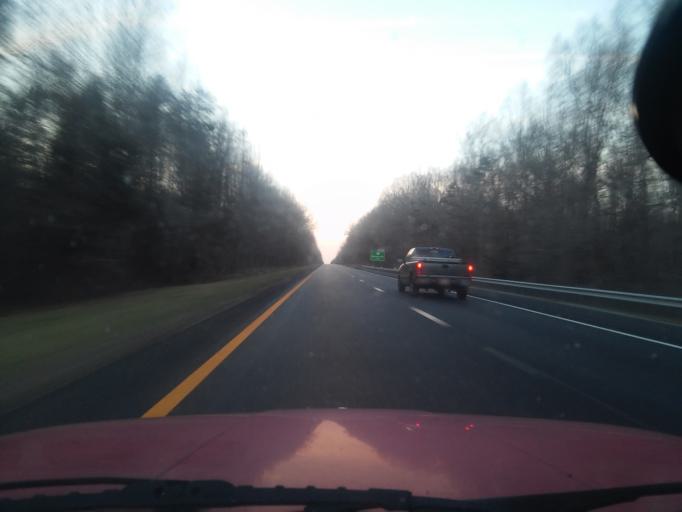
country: US
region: Virginia
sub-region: Louisa County
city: Louisa
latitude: 37.8714
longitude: -78.0147
